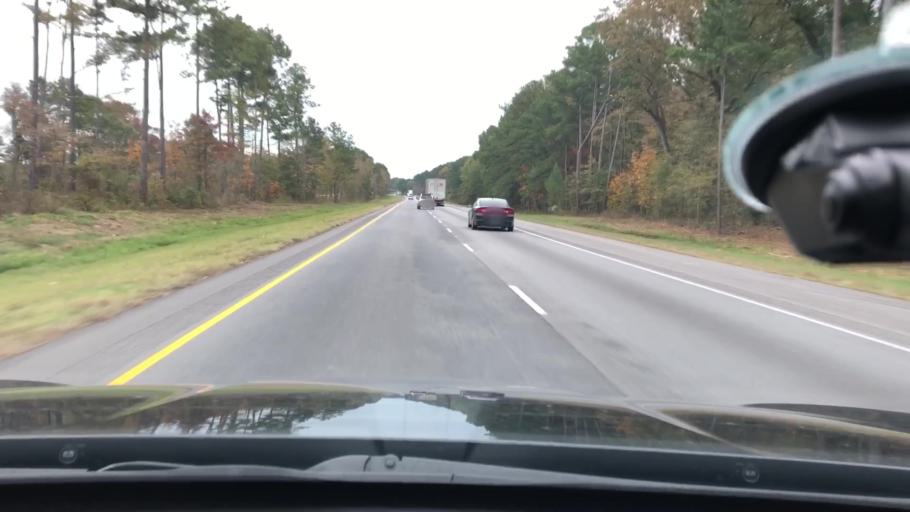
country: US
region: Arkansas
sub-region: Hempstead County
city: Hope
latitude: 33.6276
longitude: -93.7400
